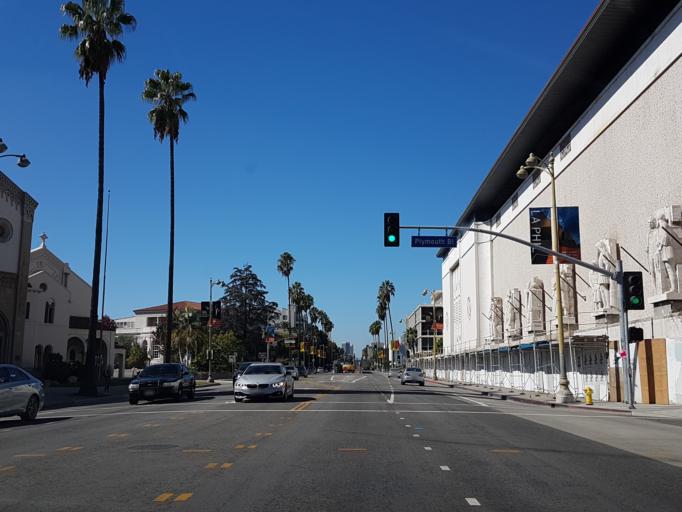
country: US
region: California
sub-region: Los Angeles County
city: Hollywood
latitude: 34.0618
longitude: -118.3227
